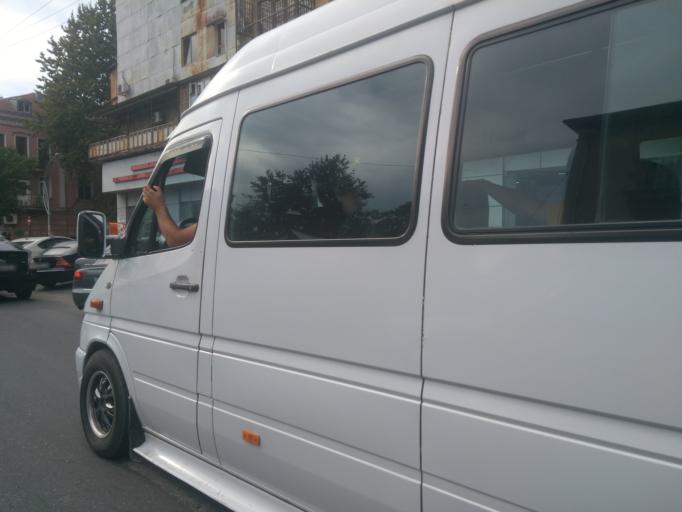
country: GE
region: Ajaria
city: Batumi
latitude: 41.6421
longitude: 41.6270
